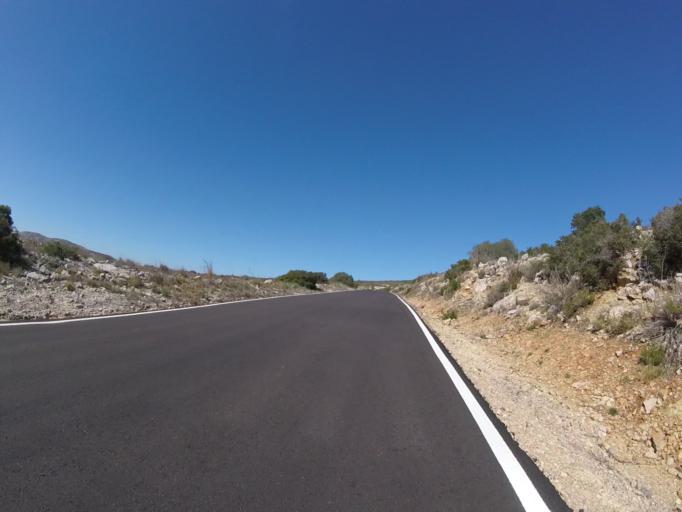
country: ES
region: Valencia
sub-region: Provincia de Castello
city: Cervera del Maestre
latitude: 40.4061
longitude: 0.2201
